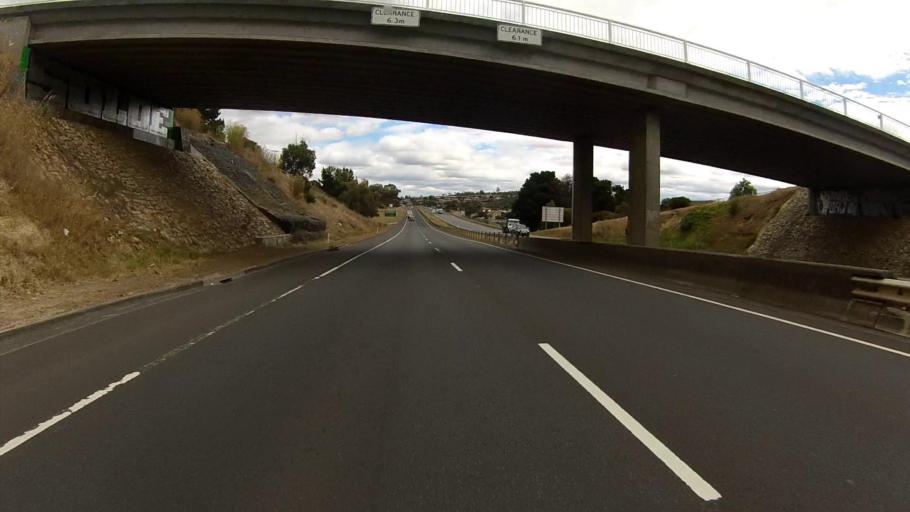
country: AU
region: Tasmania
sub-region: Glenorchy
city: Claremont
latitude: -42.7940
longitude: 147.2472
